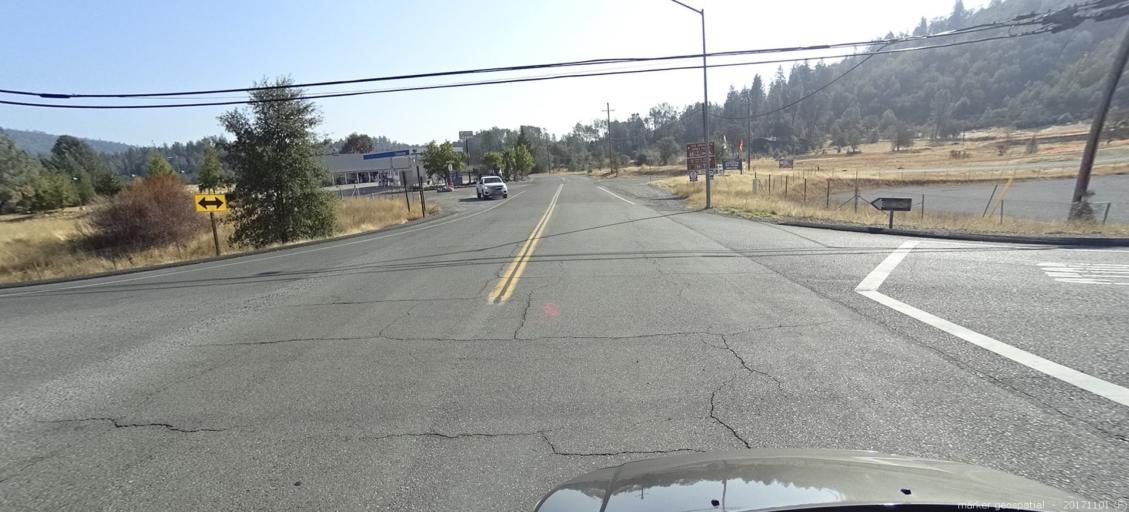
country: US
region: California
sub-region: Shasta County
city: Shasta Lake
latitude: 40.7054
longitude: -122.3360
